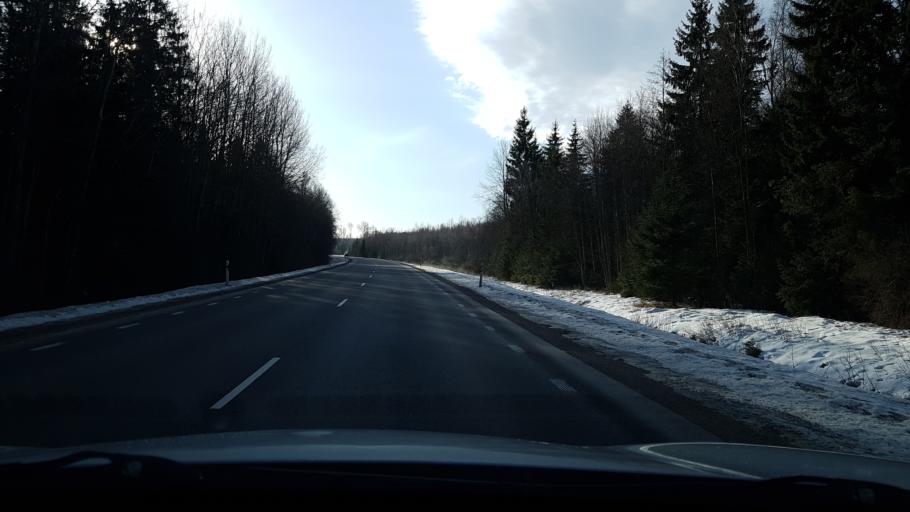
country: EE
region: Viljandimaa
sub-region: Vohma linn
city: Vohma
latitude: 58.5733
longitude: 25.5702
